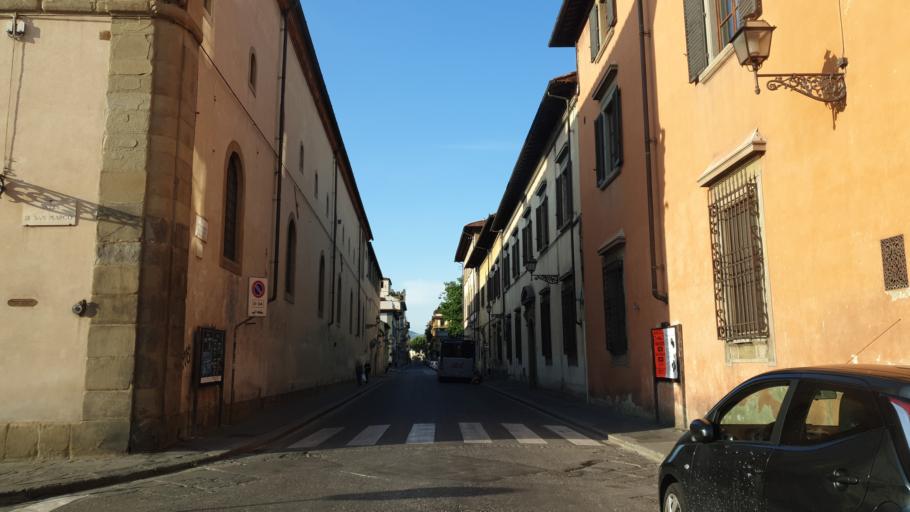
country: IT
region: Tuscany
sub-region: Province of Florence
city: Florence
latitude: 43.7778
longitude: 11.2593
